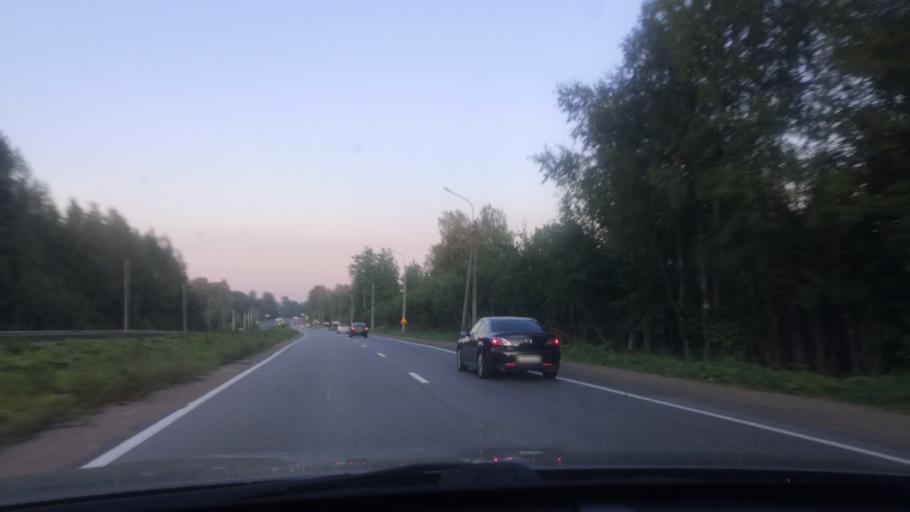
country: RU
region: St.-Petersburg
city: Beloostrov
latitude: 60.1980
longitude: 30.0155
